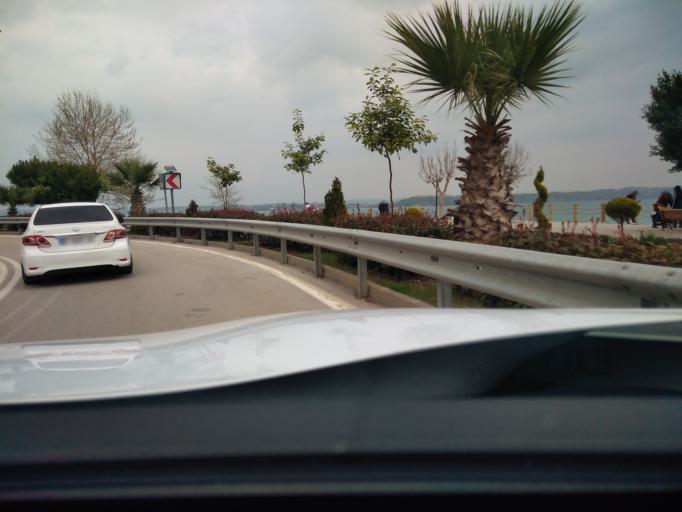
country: TR
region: Adana
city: Adana
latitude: 37.0565
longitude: 35.3066
